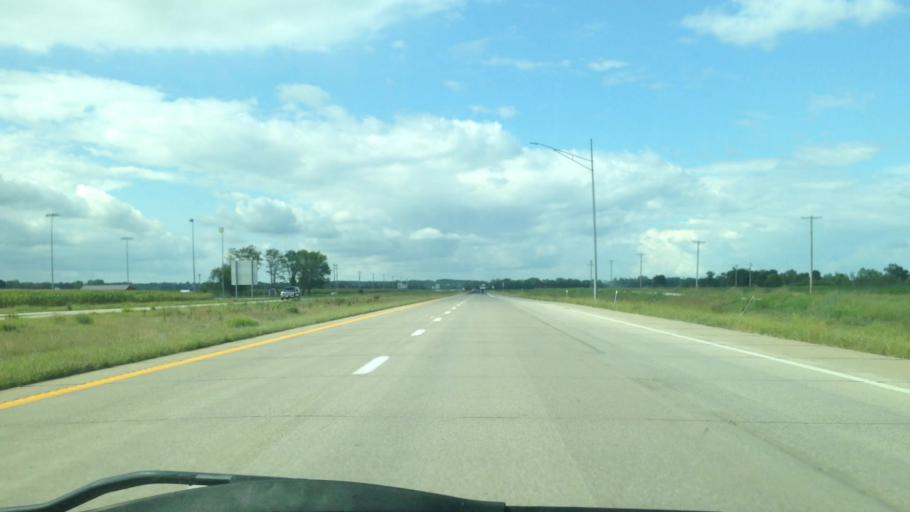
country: US
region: Illinois
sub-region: Hancock County
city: Warsaw
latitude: 40.3985
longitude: -91.5724
